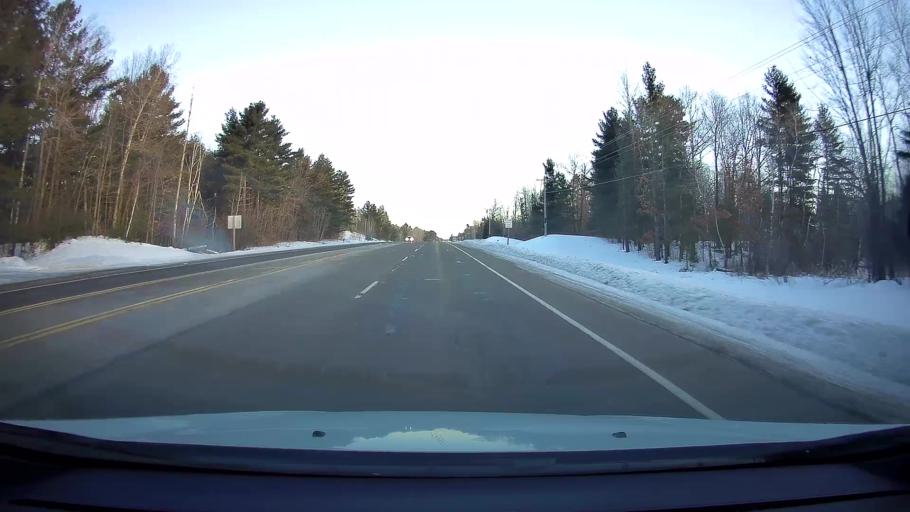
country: US
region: Wisconsin
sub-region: Barron County
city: Cumberland
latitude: 45.5611
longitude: -92.0172
